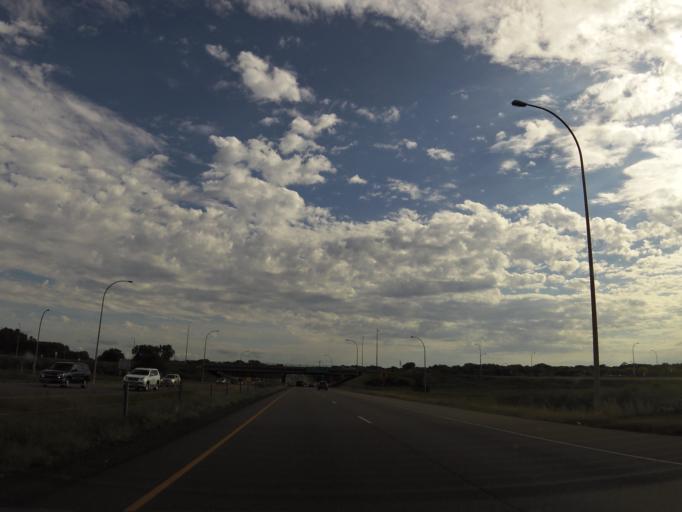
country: US
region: Minnesota
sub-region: Hennepin County
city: New Hope
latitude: 45.0352
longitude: -93.4009
